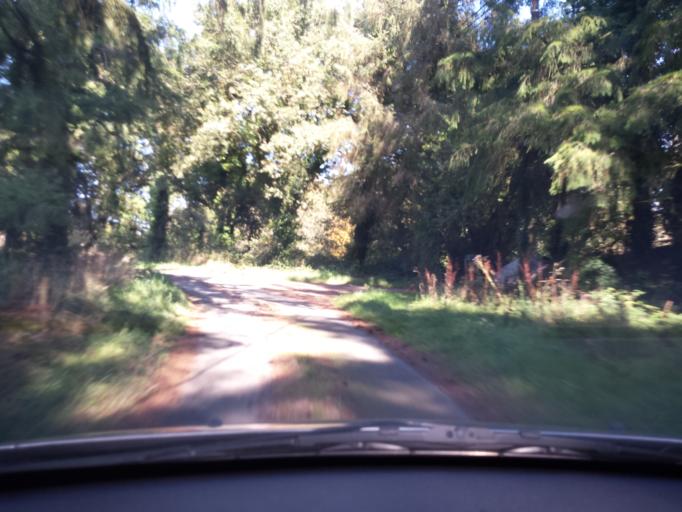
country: FR
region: Brittany
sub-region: Departement des Cotes-d'Armor
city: Plounevez-Quintin
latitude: 48.3388
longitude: -3.2494
